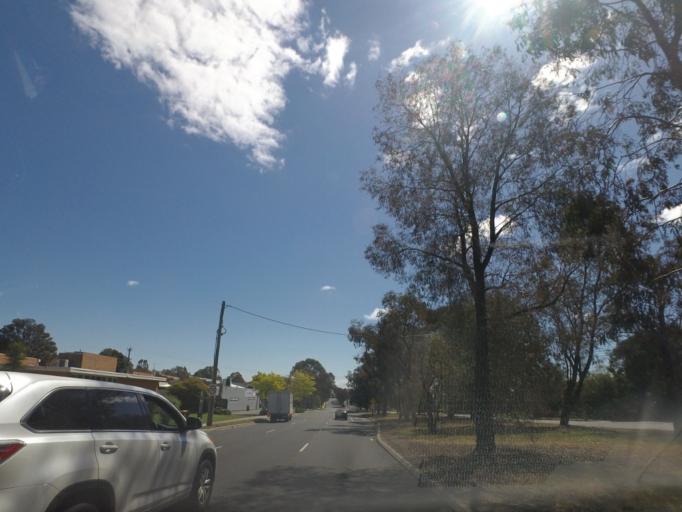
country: AU
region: Victoria
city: Clayton
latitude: -37.8981
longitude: 145.1160
